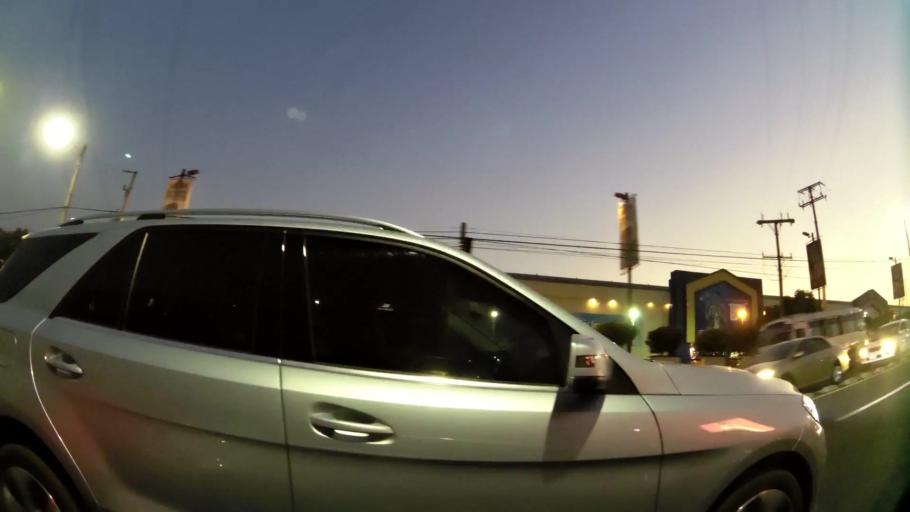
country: SV
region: La Libertad
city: Santa Tecla
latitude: 13.6797
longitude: -89.2749
